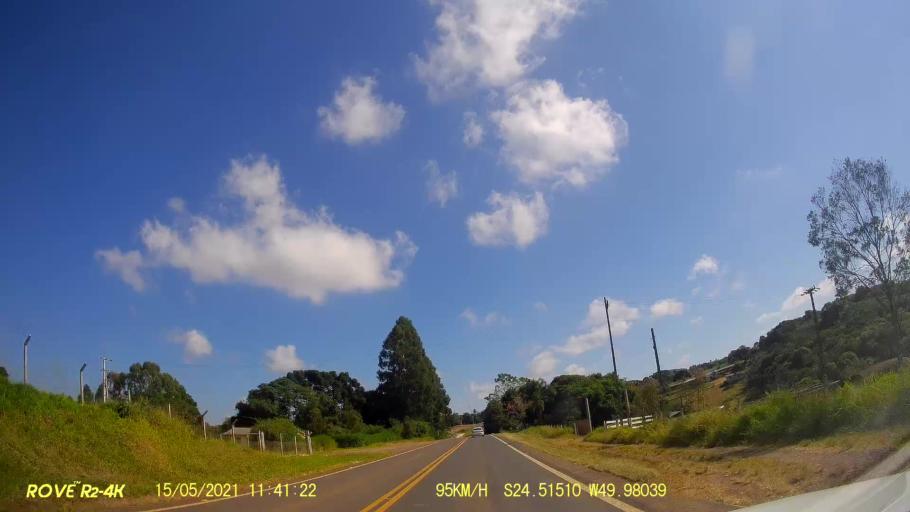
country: BR
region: Parana
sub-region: Pirai Do Sul
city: Pirai do Sul
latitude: -24.5152
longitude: -49.9803
